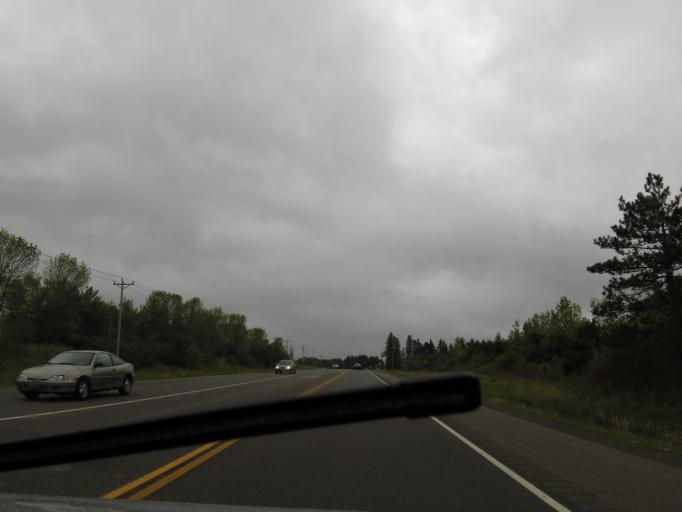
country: US
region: Minnesota
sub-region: Washington County
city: Lake Elmo
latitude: 45.0163
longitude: -92.8601
